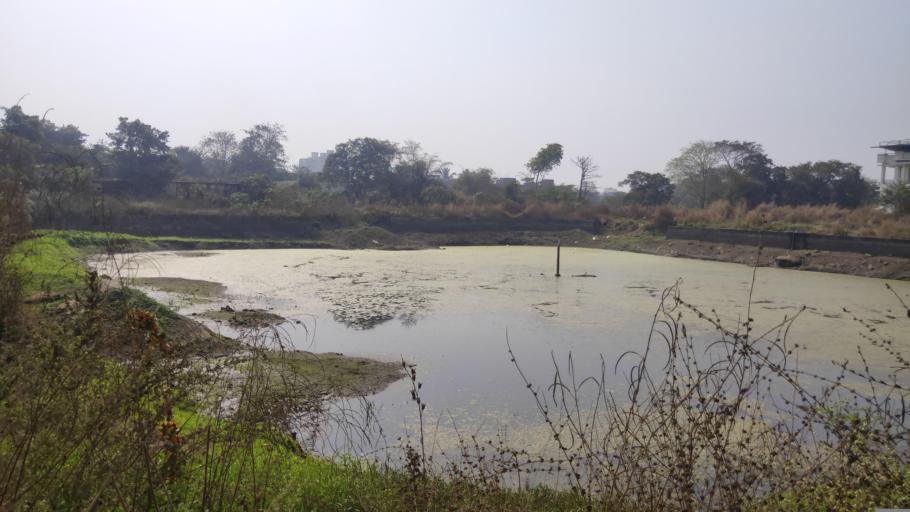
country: IN
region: Maharashtra
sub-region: Thane
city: Bhiwandi
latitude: 19.3245
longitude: 73.0674
